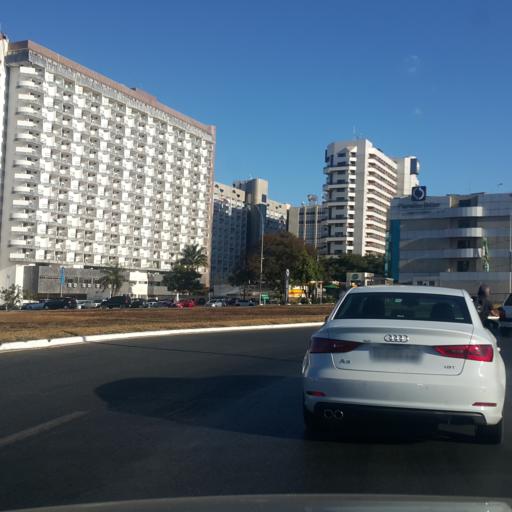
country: BR
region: Federal District
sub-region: Brasilia
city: Brasilia
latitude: -15.7926
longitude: -47.8889
